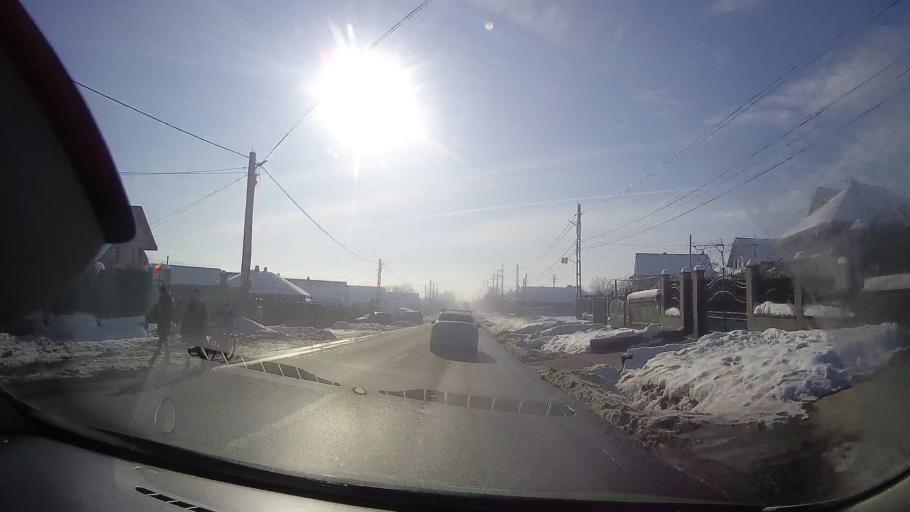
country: RO
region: Iasi
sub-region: Comuna Motca
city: Motca
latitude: 47.2527
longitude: 26.6097
